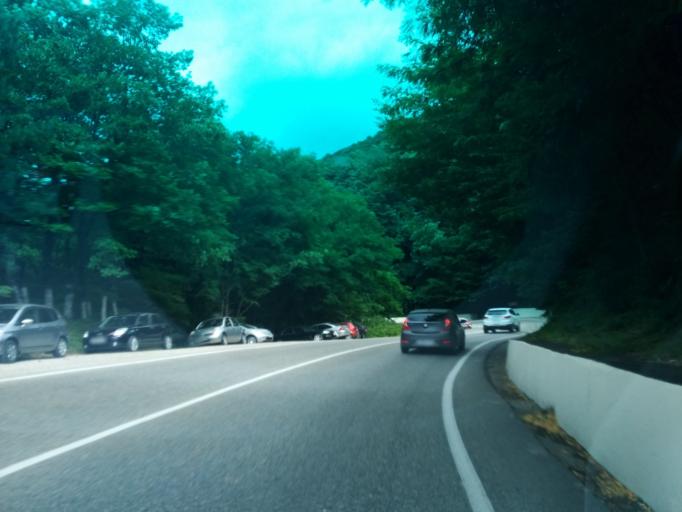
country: RU
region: Krasnodarskiy
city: Nebug
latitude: 44.1736
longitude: 38.9700
